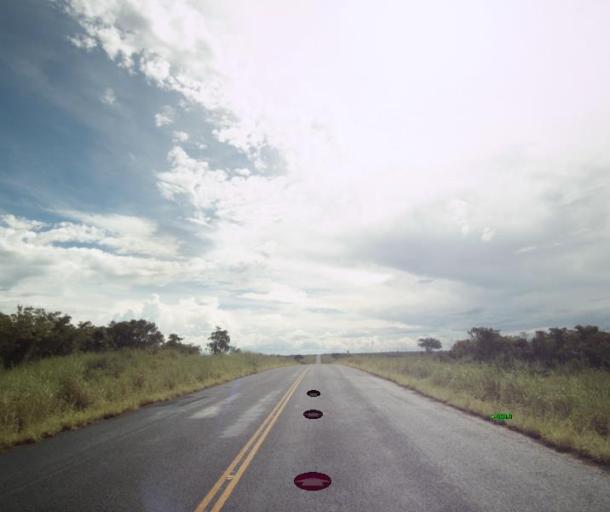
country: BR
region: Goias
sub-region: Sao Miguel Do Araguaia
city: Sao Miguel do Araguaia
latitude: -13.2973
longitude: -50.3395
